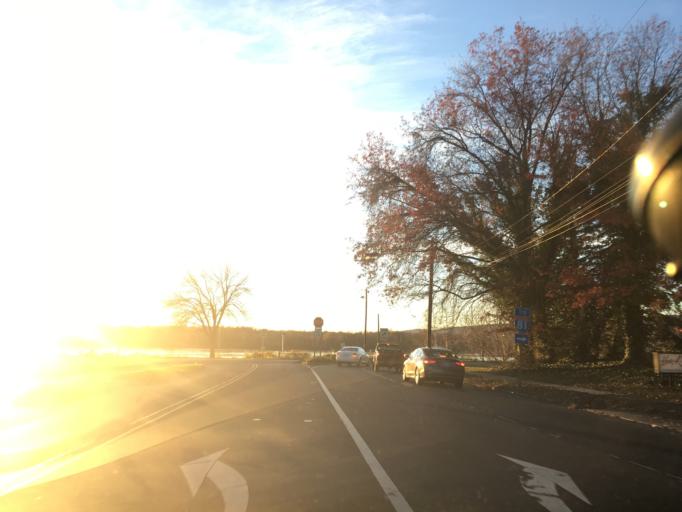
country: US
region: Pennsylvania
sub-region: Cumberland County
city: West Fairview
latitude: 40.2911
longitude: -76.9049
